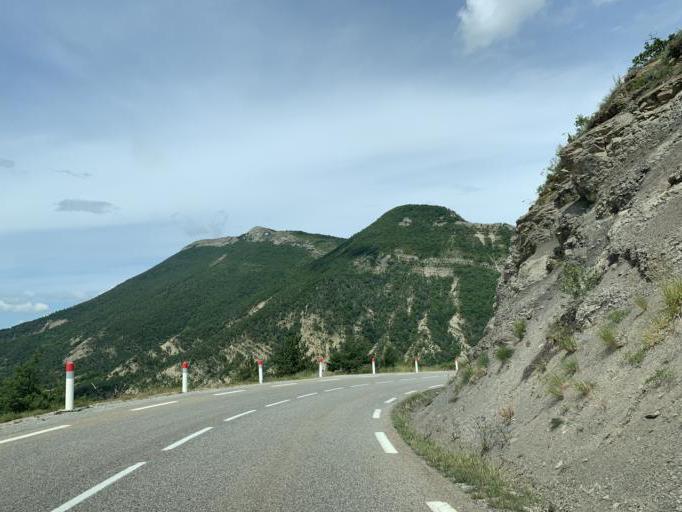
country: FR
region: Provence-Alpes-Cote d'Azur
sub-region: Departement des Hautes-Alpes
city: Veynes
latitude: 44.5381
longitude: 5.7847
